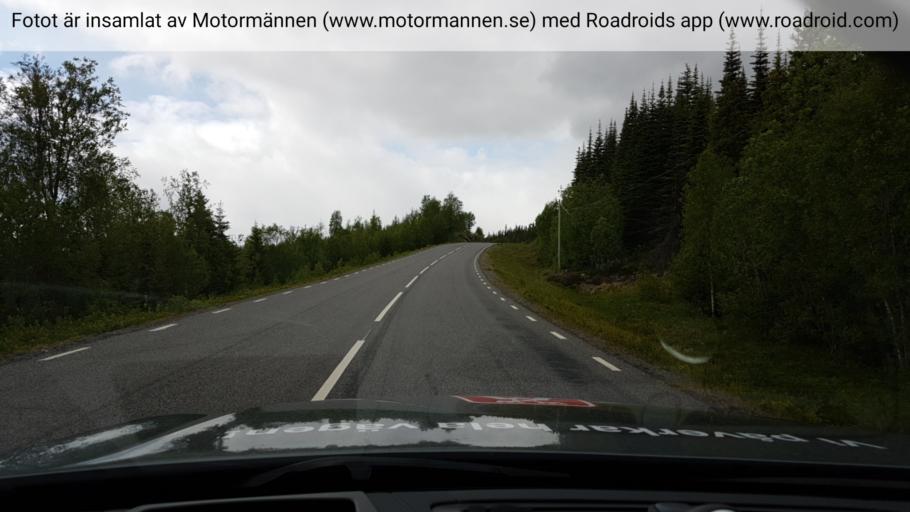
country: SE
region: Jaemtland
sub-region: Are Kommun
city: Are
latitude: 63.6419
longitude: 13.0792
